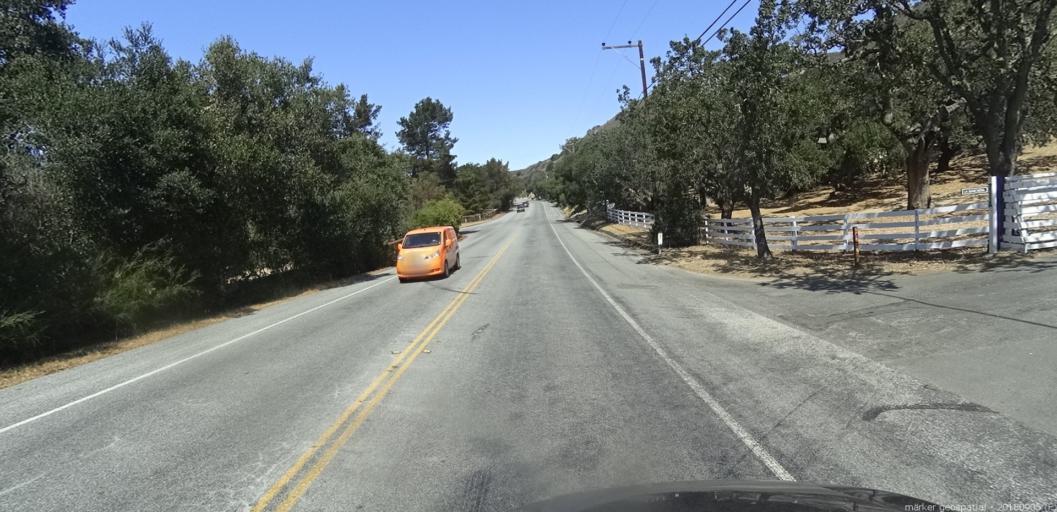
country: US
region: California
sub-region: Monterey County
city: Carmel Valley Village
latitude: 36.5066
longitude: -121.7527
